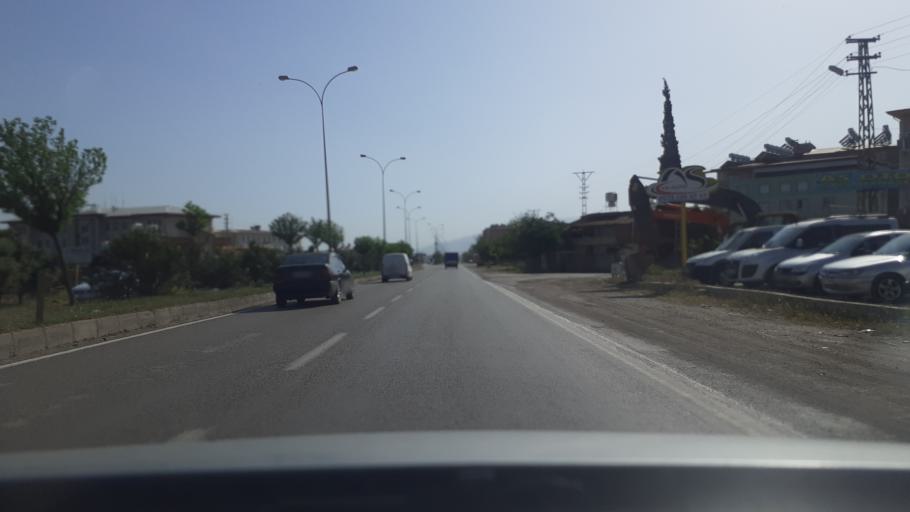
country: TR
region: Hatay
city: Kirikhan
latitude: 36.4853
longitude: 36.3633
